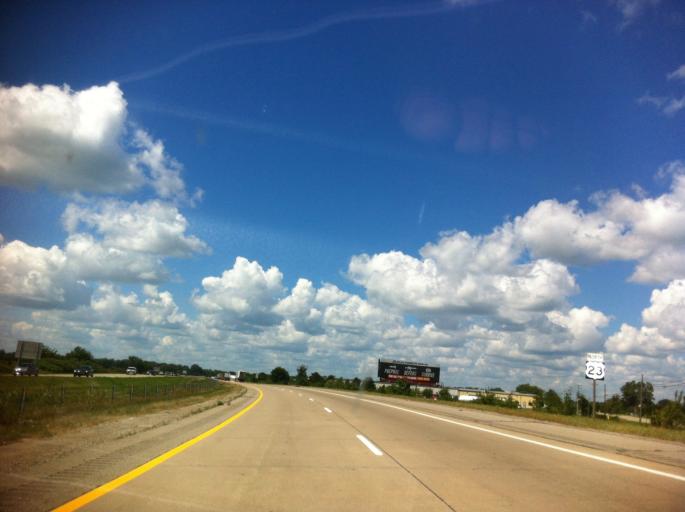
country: US
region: Michigan
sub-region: Monroe County
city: Dundee
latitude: 41.9663
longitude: -83.6730
